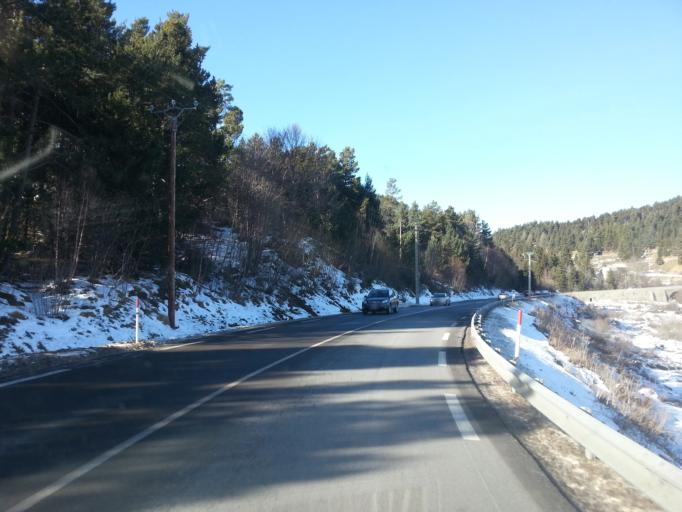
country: ES
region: Catalonia
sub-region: Provincia de Girona
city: Llivia
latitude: 42.5123
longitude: 2.1133
